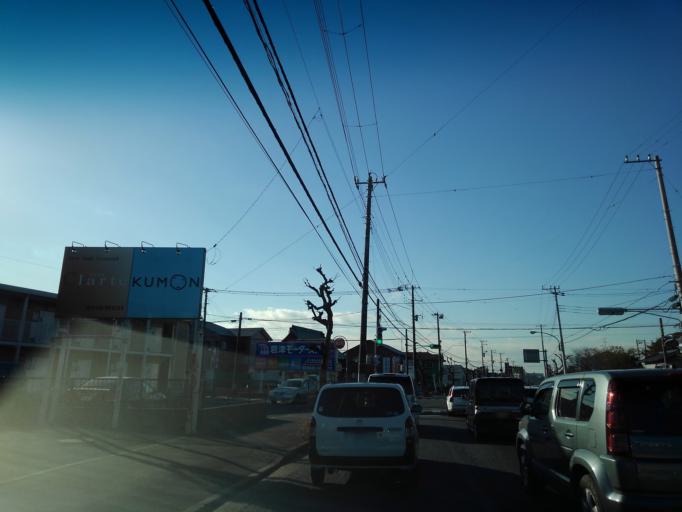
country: JP
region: Chiba
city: Kimitsu
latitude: 35.3292
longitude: 139.8979
